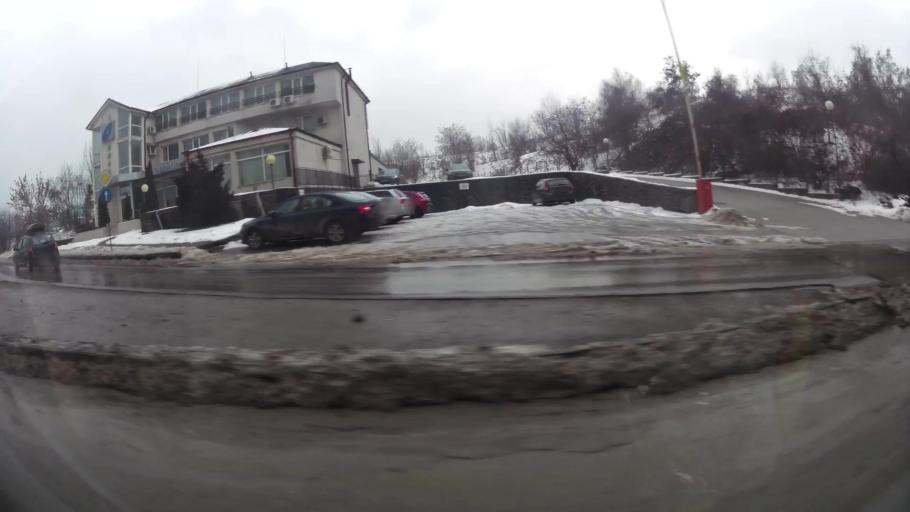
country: BG
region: Sofiya
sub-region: Obshtina Bozhurishte
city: Bozhurishte
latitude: 42.6846
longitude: 23.2403
